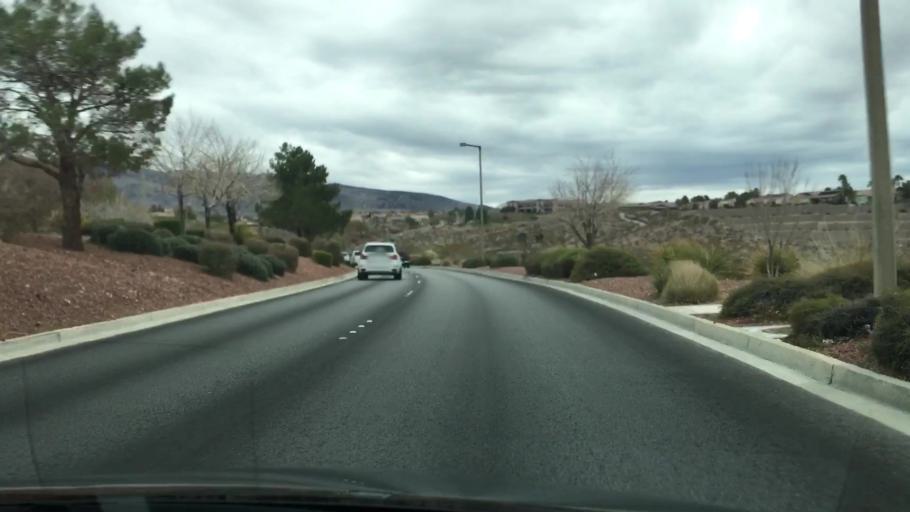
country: US
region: Nevada
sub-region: Clark County
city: Whitney
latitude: 35.9639
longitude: -115.0978
